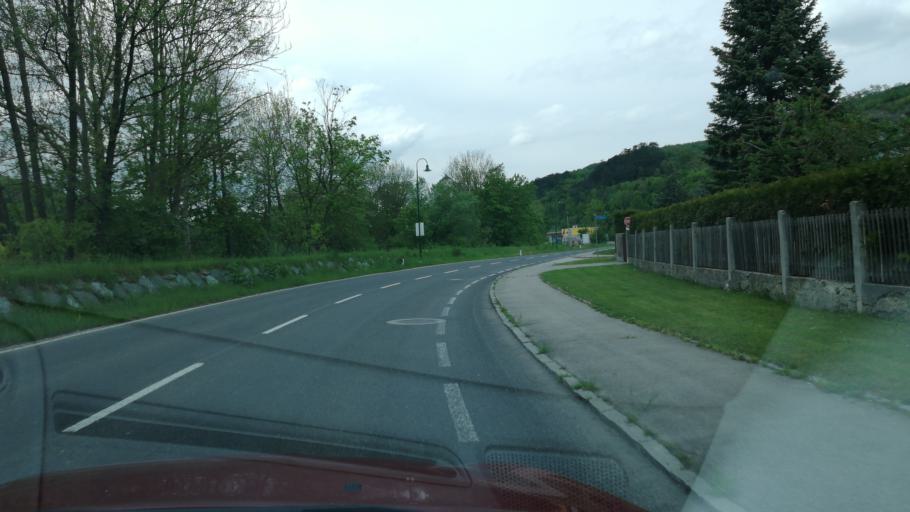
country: AT
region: Lower Austria
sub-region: Politischer Bezirk Baden
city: Alland
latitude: 48.0582
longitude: 16.0747
